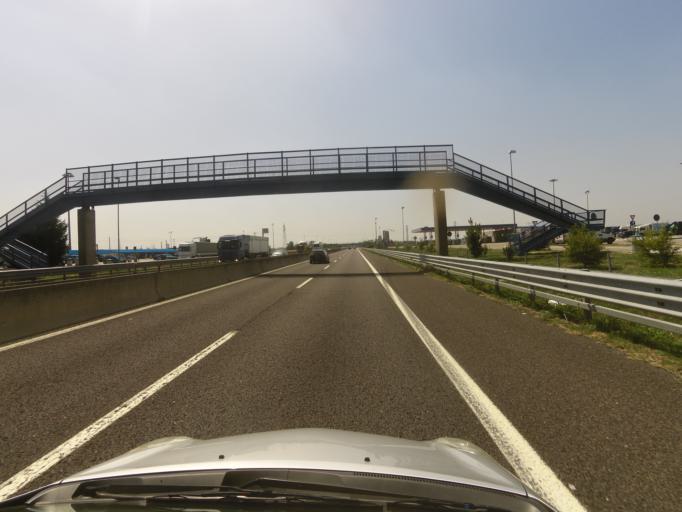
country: IT
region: Emilia-Romagna
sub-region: Provincia di Ferrara
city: Porotto-Cassama
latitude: 44.8801
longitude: 11.5700
